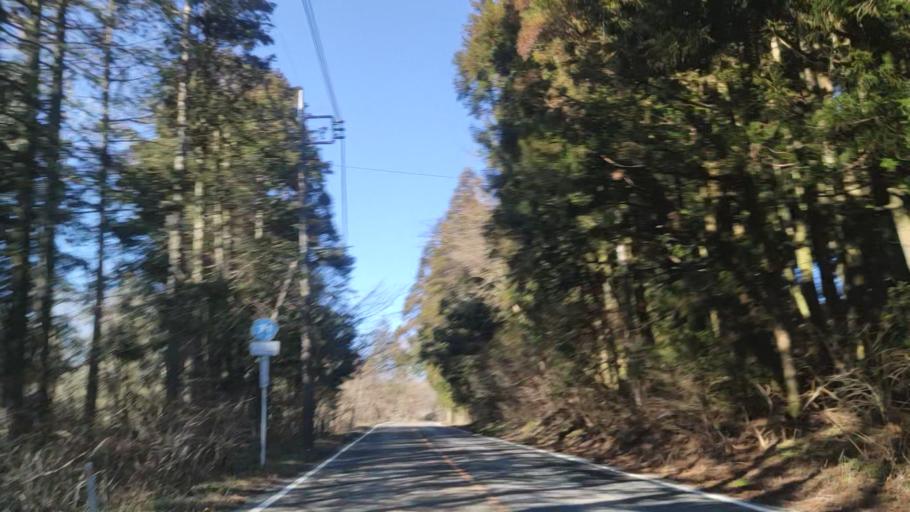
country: JP
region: Yamanashi
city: Fujikawaguchiko
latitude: 35.3973
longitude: 138.6110
